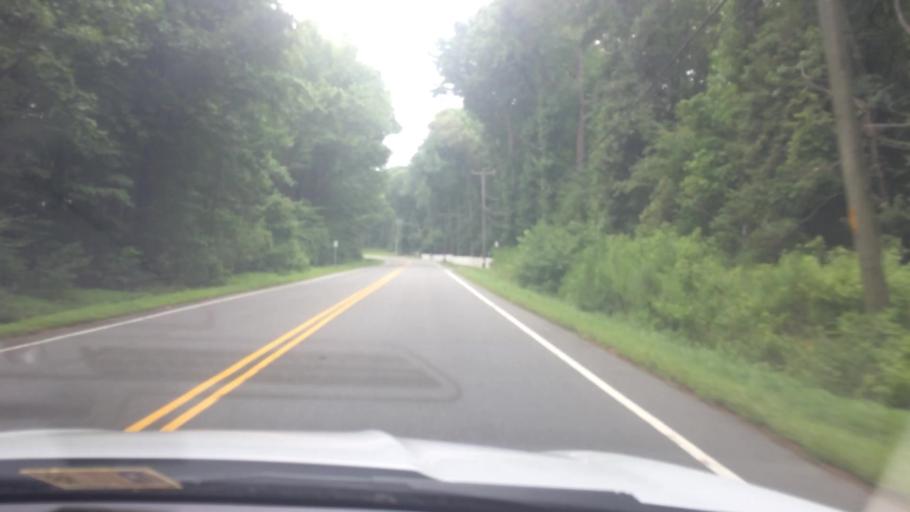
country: US
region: Virginia
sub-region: York County
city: Yorktown
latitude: 37.2342
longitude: -76.5365
